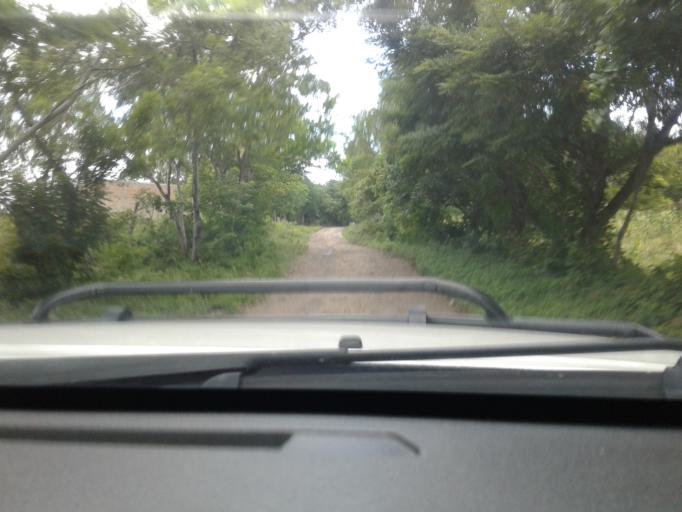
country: NI
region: Leon
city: Santa Rosa del Penon
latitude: 12.9027
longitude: -86.2219
